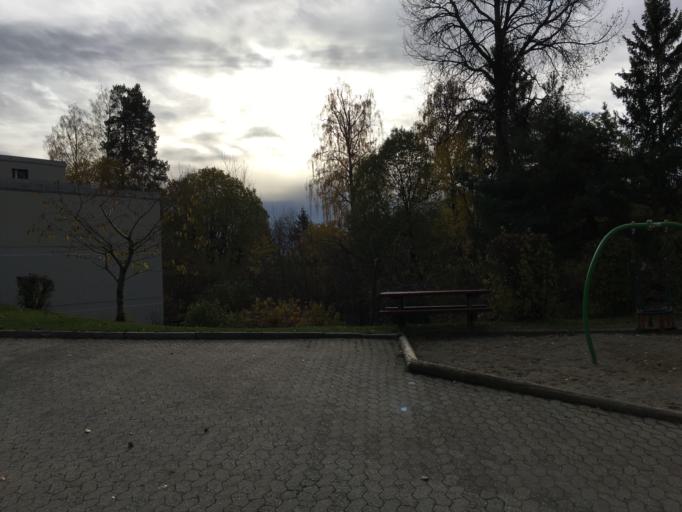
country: NO
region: Akershus
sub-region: Baerum
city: Lysaker
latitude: 59.9385
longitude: 10.6343
